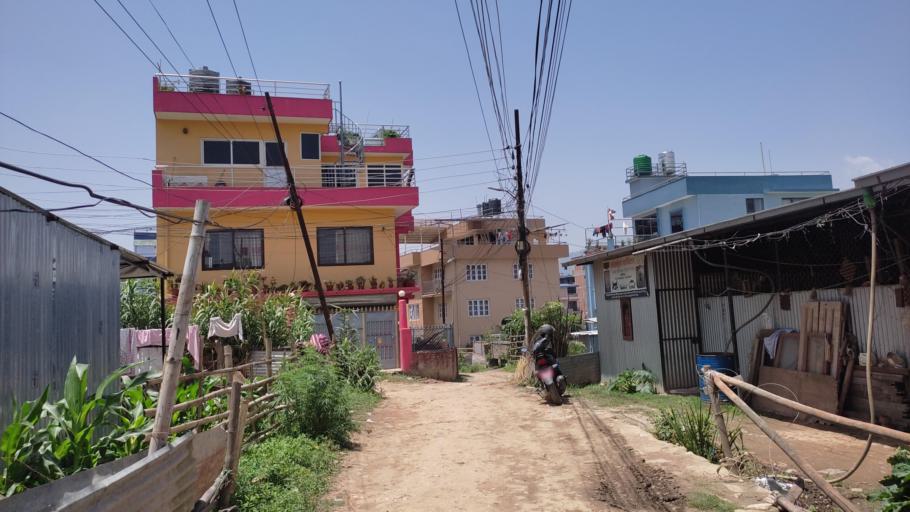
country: NP
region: Central Region
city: Kirtipur
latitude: 27.6732
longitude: 85.2734
